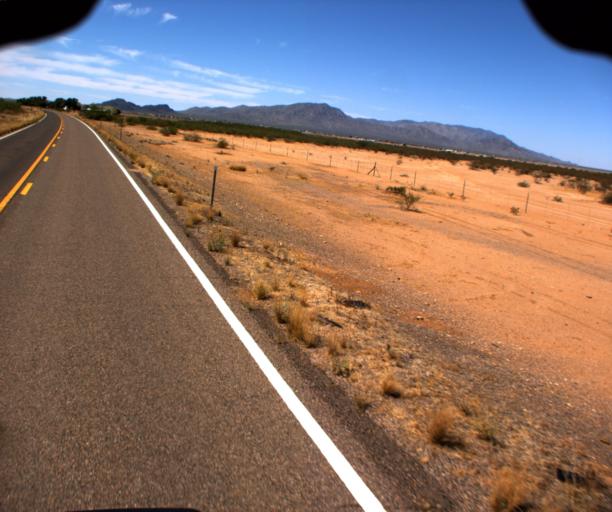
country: US
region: Arizona
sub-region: Yavapai County
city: Congress
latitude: 33.9775
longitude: -113.1407
